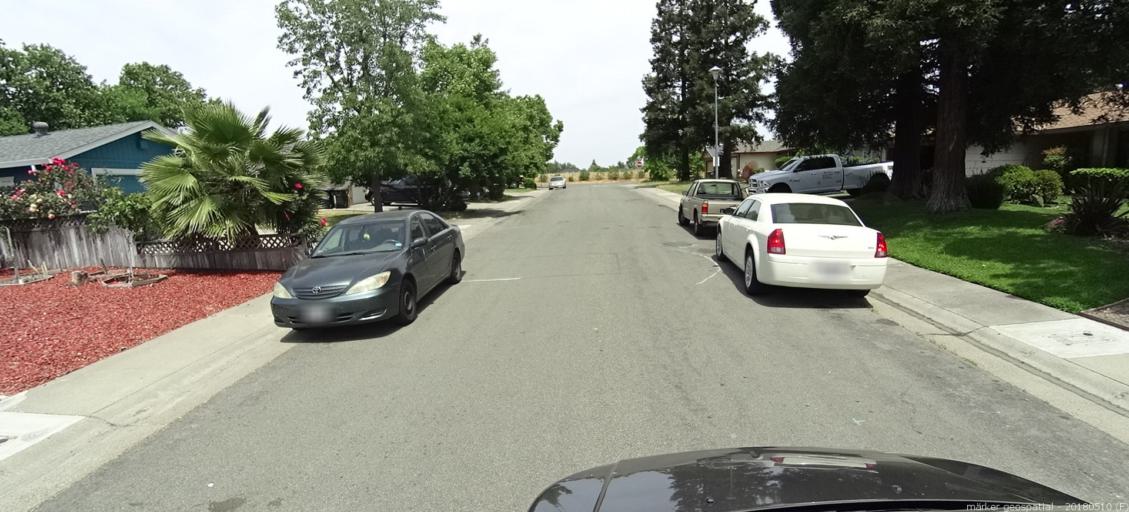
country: US
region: California
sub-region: Sacramento County
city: Rio Linda
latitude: 38.6505
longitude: -121.4555
